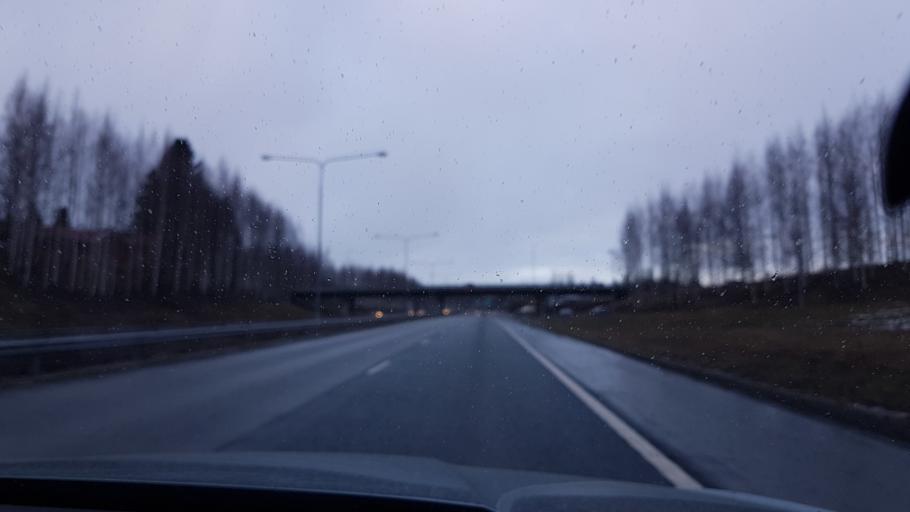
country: FI
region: Pirkanmaa
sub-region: Tampere
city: Tampere
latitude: 61.4868
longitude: 23.8743
